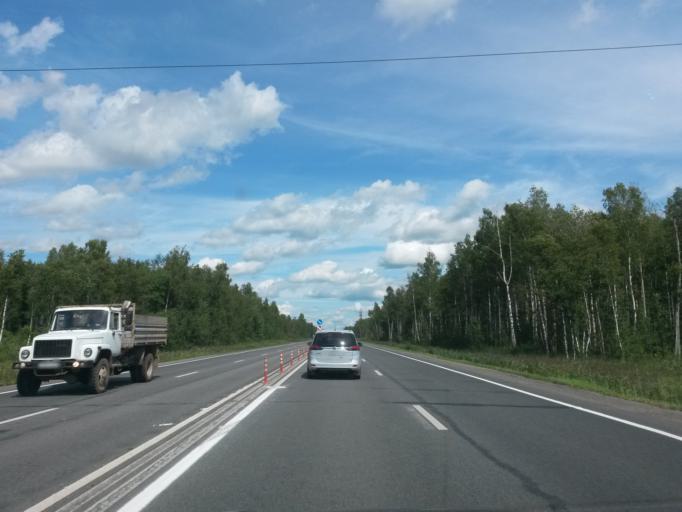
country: RU
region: Jaroslavl
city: Rostov
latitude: 57.2306
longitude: 39.4676
